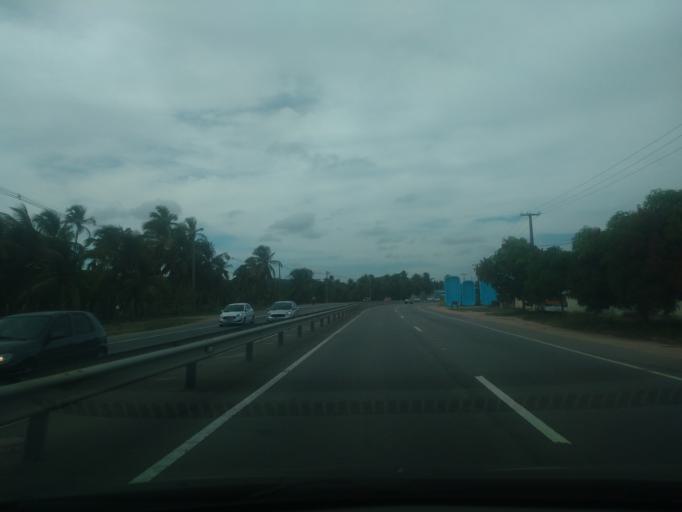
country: BR
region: Alagoas
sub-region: Marechal Deodoro
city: Marechal Deodoro
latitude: -9.7159
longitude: -35.8255
